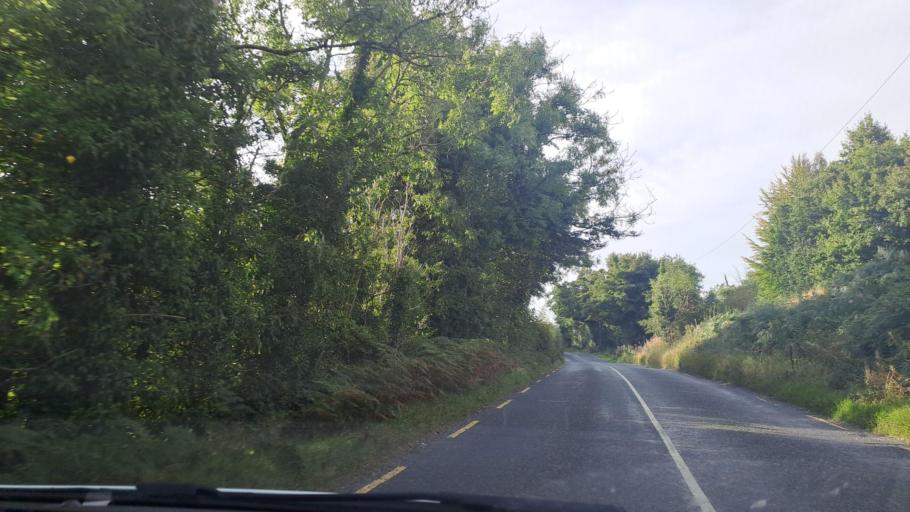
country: IE
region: Ulster
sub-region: An Cabhan
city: Bailieborough
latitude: 53.9877
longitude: -6.8845
